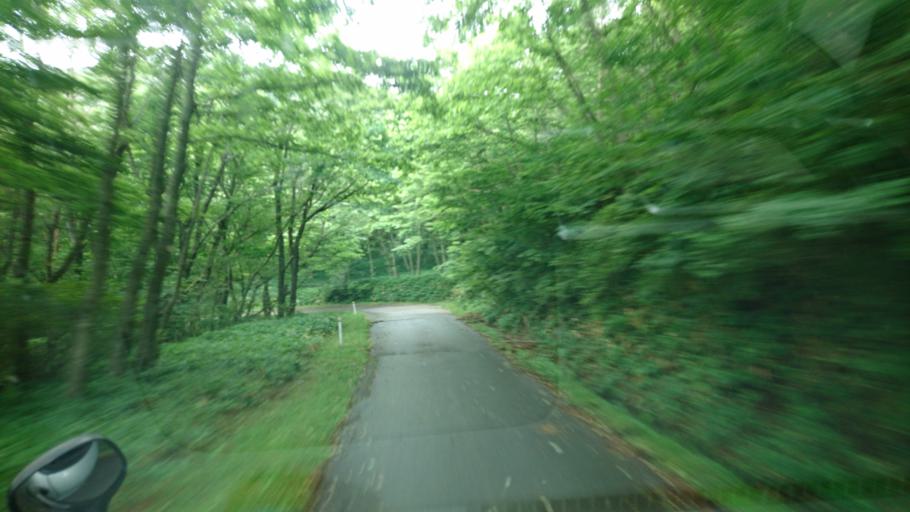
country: JP
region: Iwate
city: Ofunato
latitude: 39.1383
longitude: 141.7546
